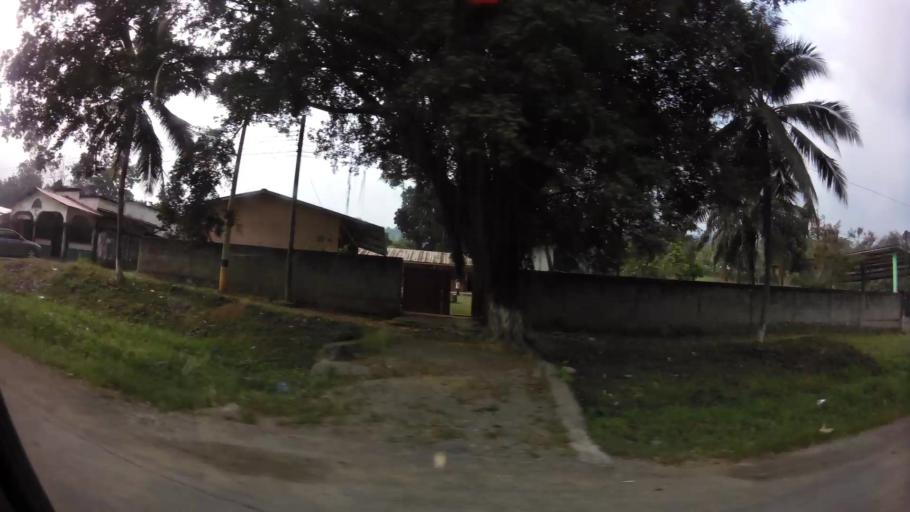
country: HN
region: Yoro
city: Guaimitas
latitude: 15.5107
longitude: -87.6809
